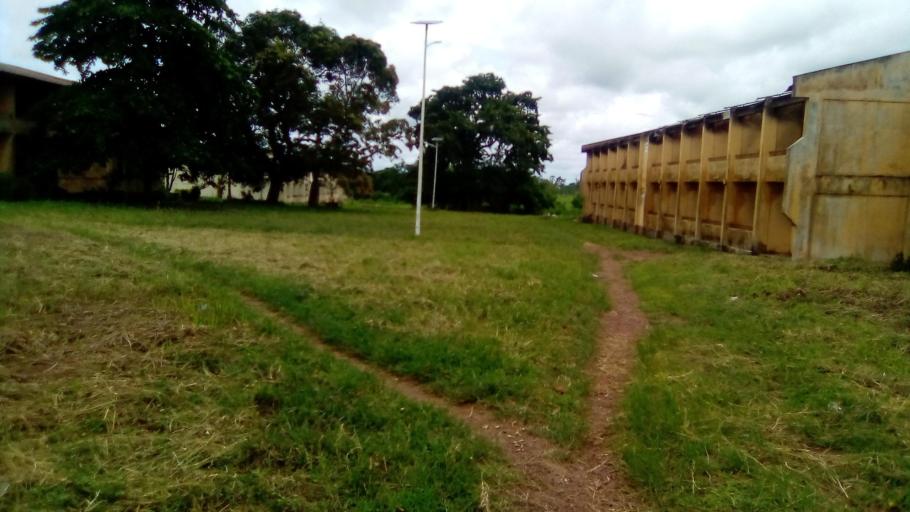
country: SL
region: Southern Province
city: Largo
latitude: 8.1191
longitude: -12.0696
